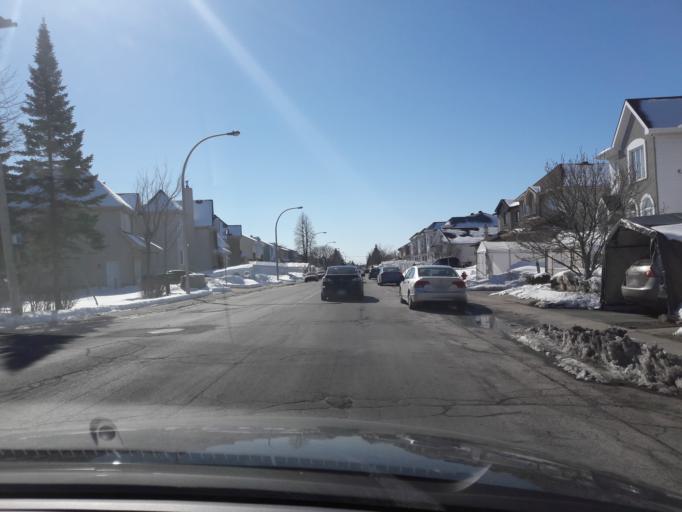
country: CA
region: Quebec
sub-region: Laurentides
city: Rosemere
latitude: 45.5590
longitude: -73.7790
